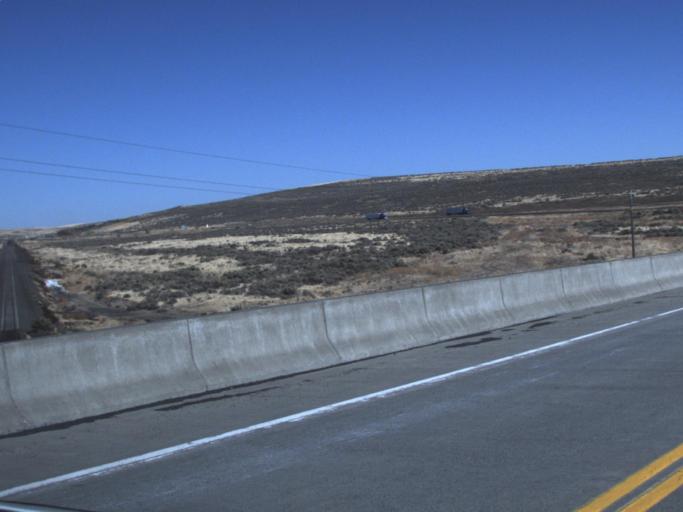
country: US
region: Washington
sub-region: Adams County
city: Ritzville
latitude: 46.9701
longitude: -118.5740
